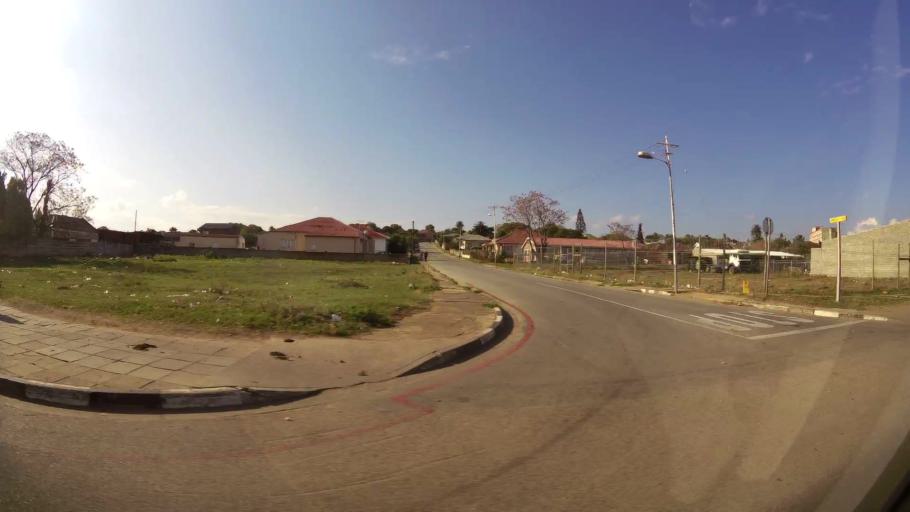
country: ZA
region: Eastern Cape
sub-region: Nelson Mandela Bay Metropolitan Municipality
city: Uitenhage
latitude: -33.7614
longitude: 25.3917
